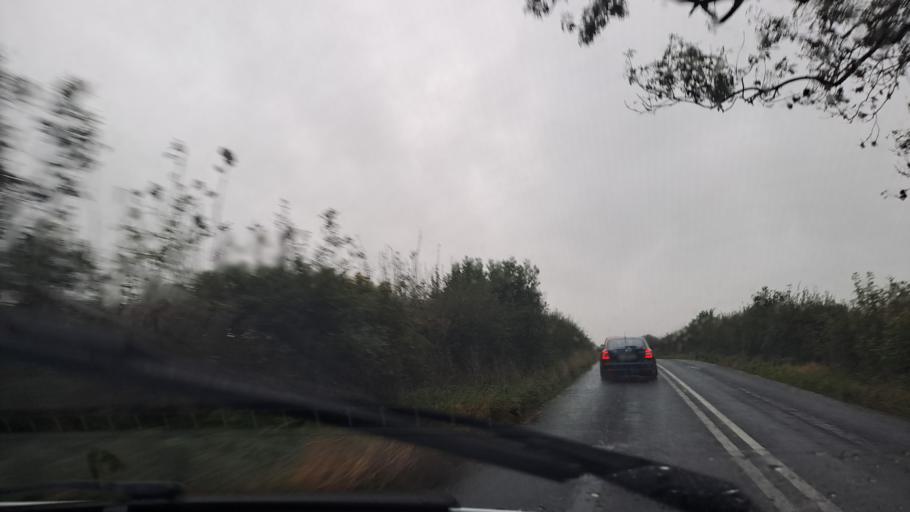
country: IE
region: Leinster
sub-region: Lu
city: Dundalk
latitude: 53.9901
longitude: -6.4733
